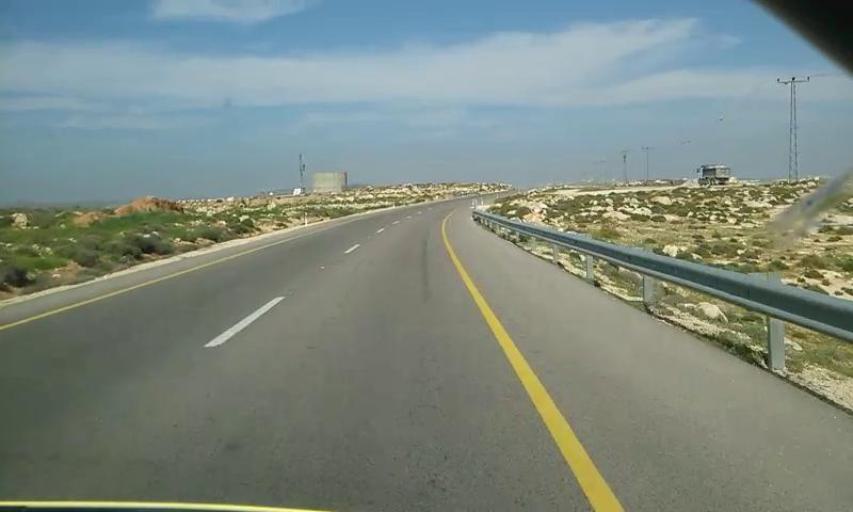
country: PS
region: West Bank
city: As Samu`
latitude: 31.3980
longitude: 35.0292
